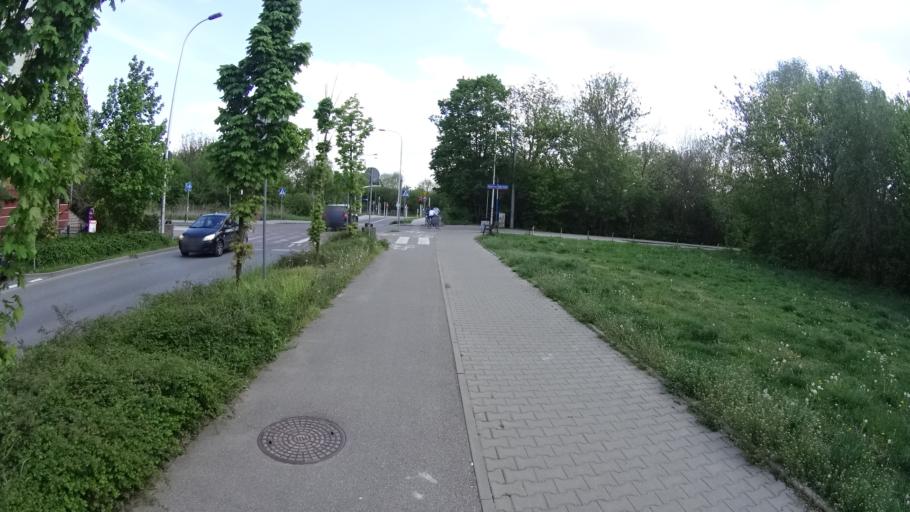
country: PL
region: Masovian Voivodeship
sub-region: Warszawa
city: Mokotow
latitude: 52.2091
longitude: 21.0589
